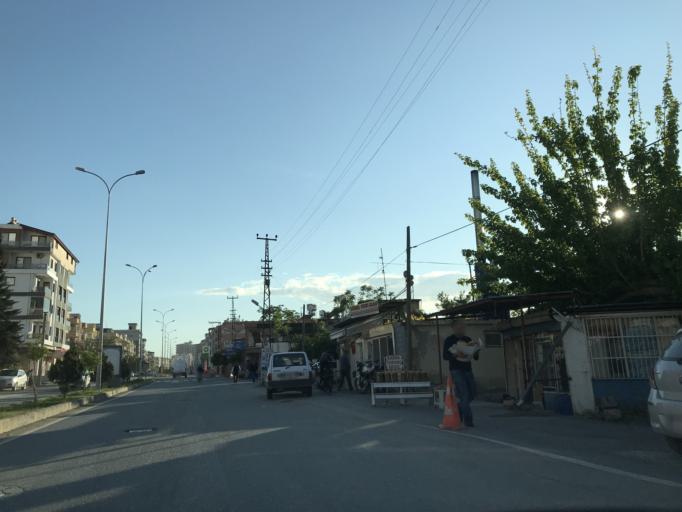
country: TR
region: Hatay
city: Iskenderun
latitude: 36.5699
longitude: 36.1525
